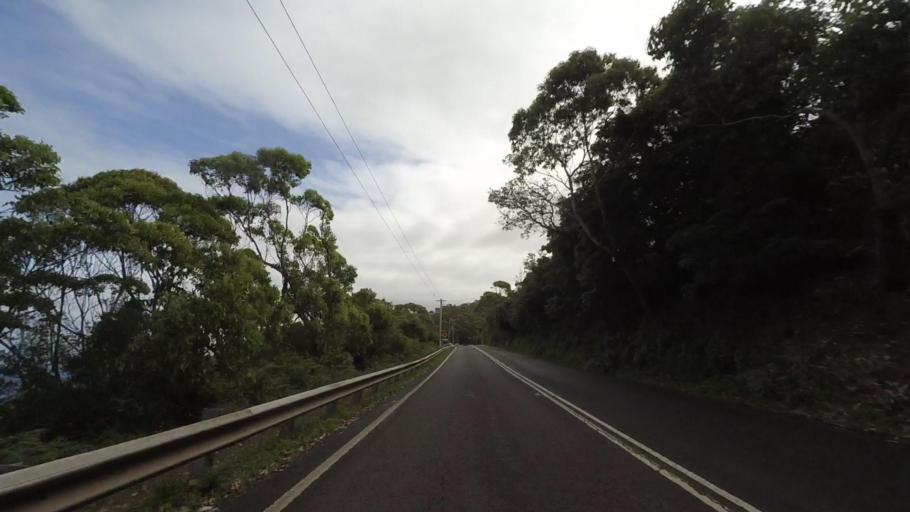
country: AU
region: New South Wales
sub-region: Wollongong
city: Helensburgh
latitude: -34.2130
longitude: 151.0079
